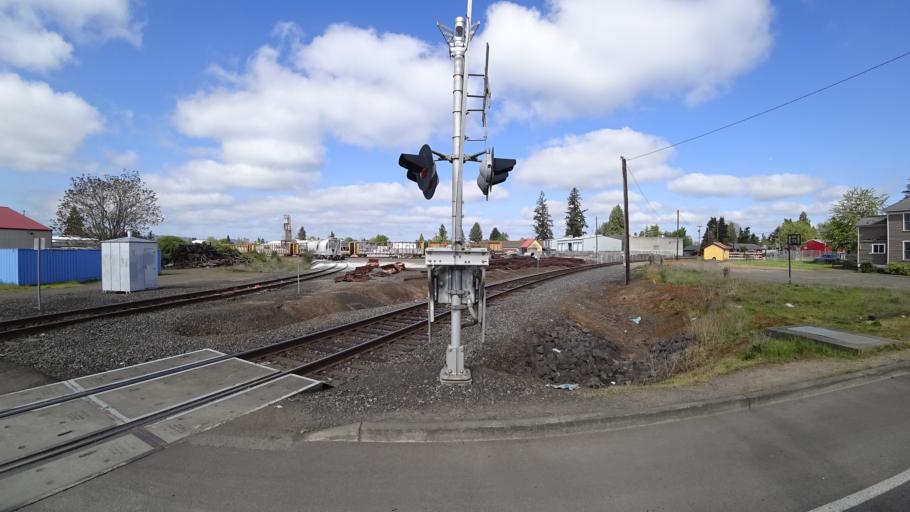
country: US
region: Oregon
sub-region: Washington County
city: Hillsboro
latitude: 45.5166
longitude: -122.9900
